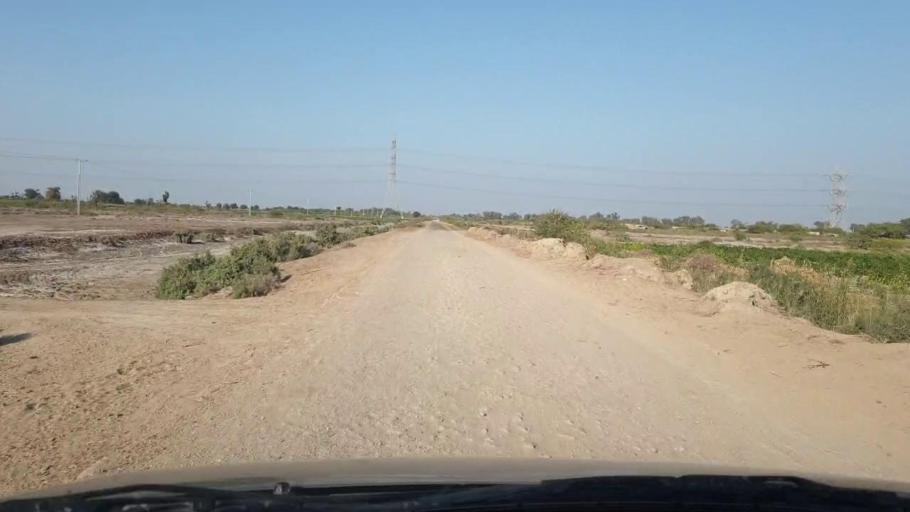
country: PK
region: Sindh
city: Samaro
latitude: 25.1497
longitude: 69.3086
